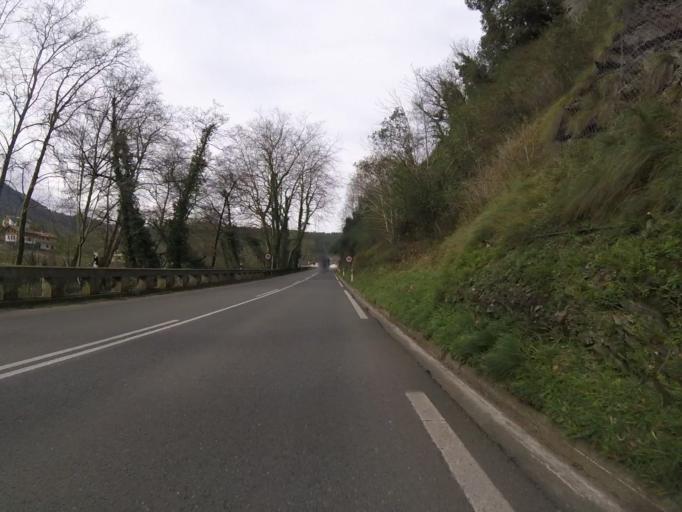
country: ES
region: Basque Country
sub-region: Provincia de Guipuzcoa
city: Aizarnazabal
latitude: 43.2593
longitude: -2.2338
